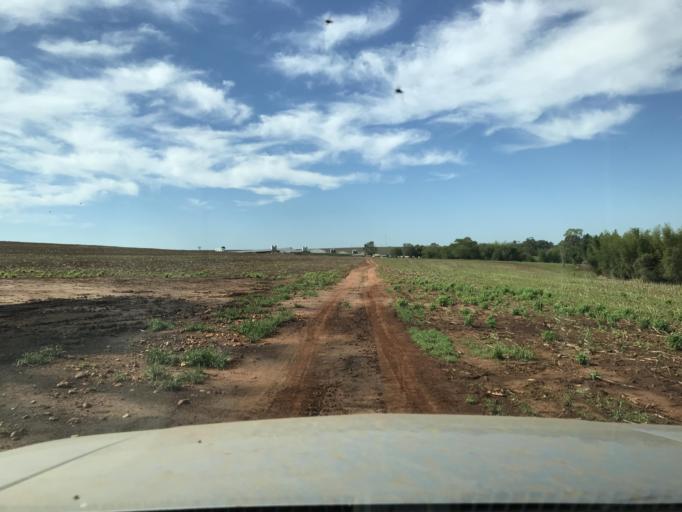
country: BR
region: Parana
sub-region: Palotina
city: Palotina
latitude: -24.1749
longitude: -53.8389
